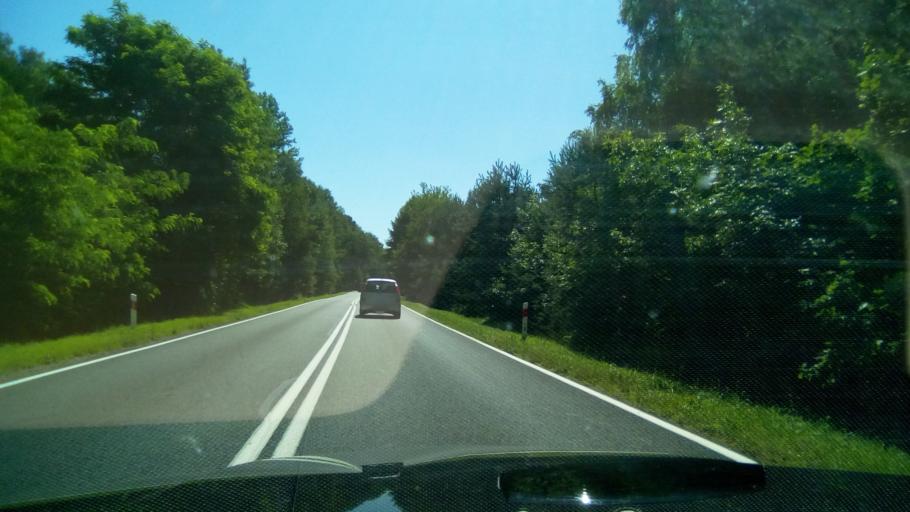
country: PL
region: Lodz Voivodeship
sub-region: Powiat tomaszowski
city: Inowlodz
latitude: 51.5262
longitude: 20.1888
